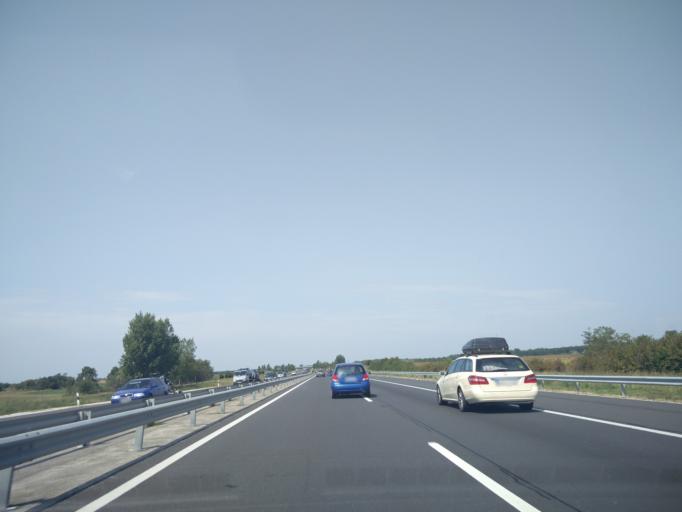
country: HU
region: Bacs-Kiskun
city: Kiskunfelegyhaza
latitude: 46.7360
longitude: 19.7853
